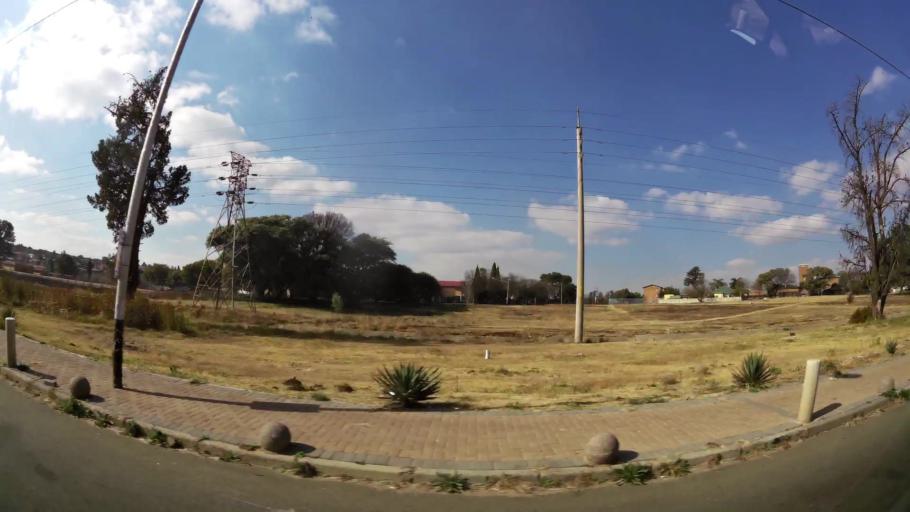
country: ZA
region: Gauteng
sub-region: West Rand District Municipality
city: Krugersdorp
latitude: -26.0983
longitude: 27.7635
